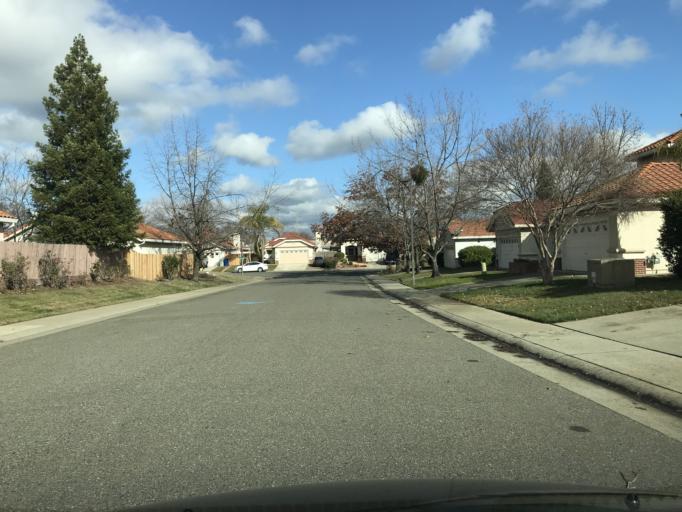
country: US
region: California
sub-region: Sacramento County
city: Folsom
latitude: 38.6614
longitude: -121.1373
